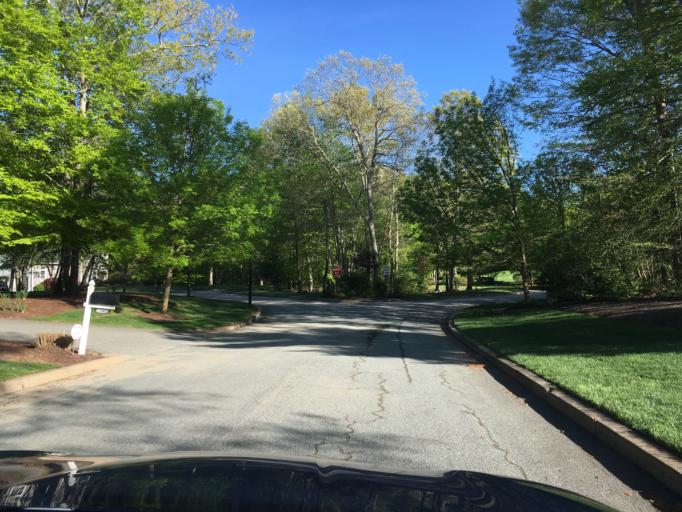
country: US
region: Rhode Island
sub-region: Washington County
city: Exeter
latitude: 41.6090
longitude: -71.5225
